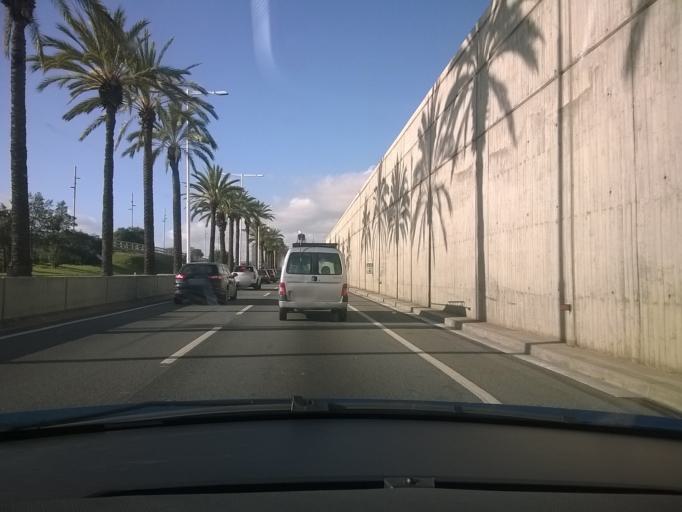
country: ES
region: Catalonia
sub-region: Provincia de Barcelona
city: Sant Marti
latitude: 41.4059
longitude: 2.2178
